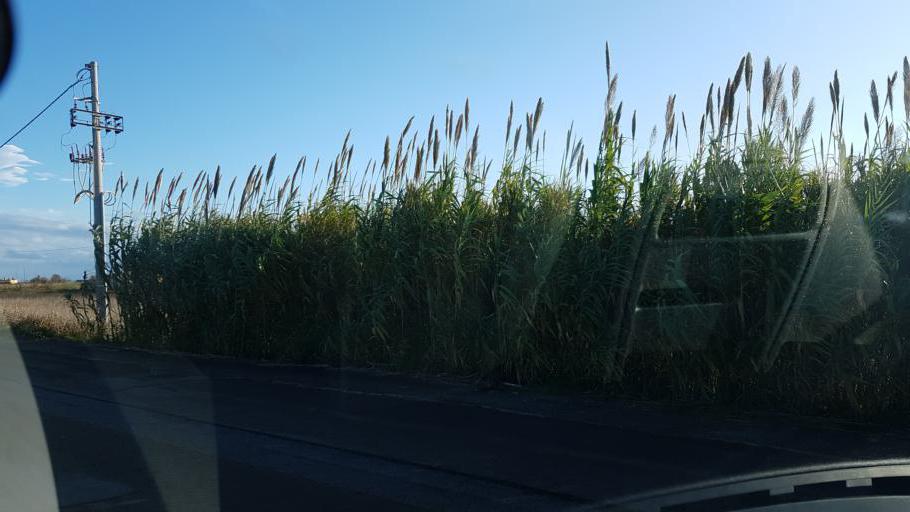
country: IT
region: Apulia
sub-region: Provincia di Brindisi
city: Torchiarolo
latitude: 40.5324
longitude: 18.0709
